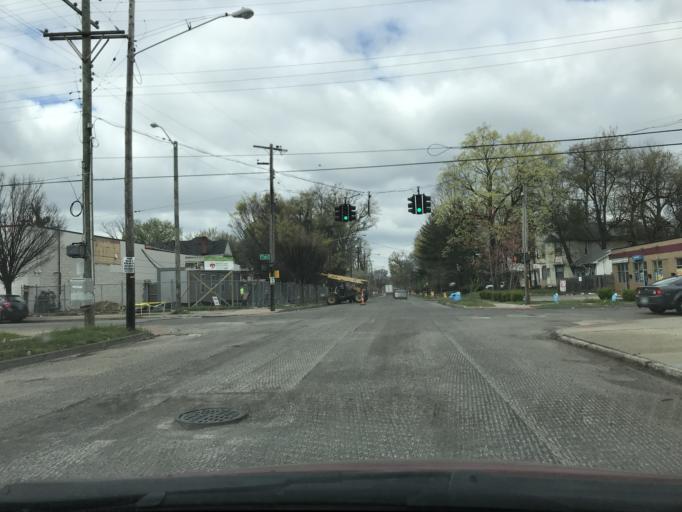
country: US
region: Kentucky
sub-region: Jefferson County
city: Louisville
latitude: 38.2381
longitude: -85.8000
